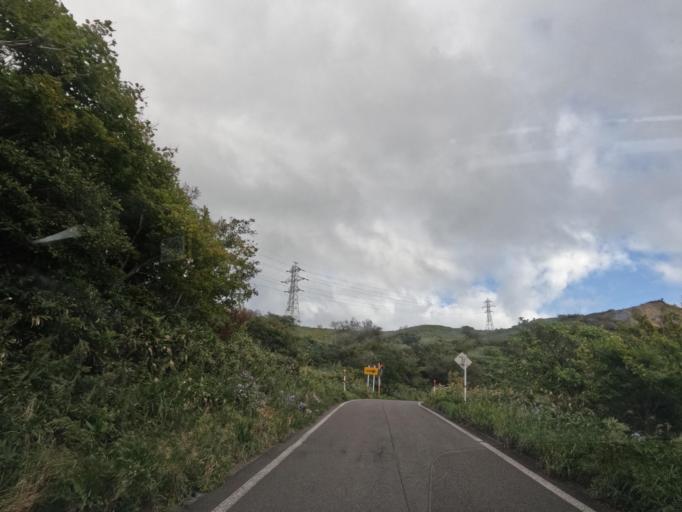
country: JP
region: Hokkaido
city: Muroran
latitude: 42.3251
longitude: 141.0035
